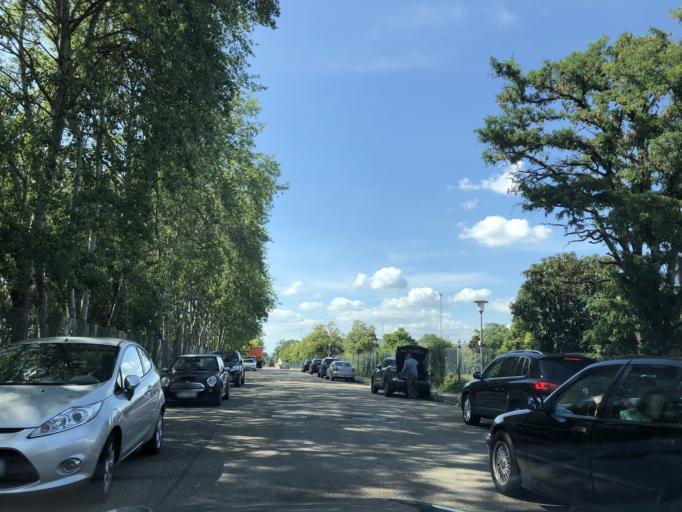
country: DE
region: Baden-Wuerttemberg
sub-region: Karlsruhe Region
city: Rastatt
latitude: 48.8553
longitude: 8.2287
